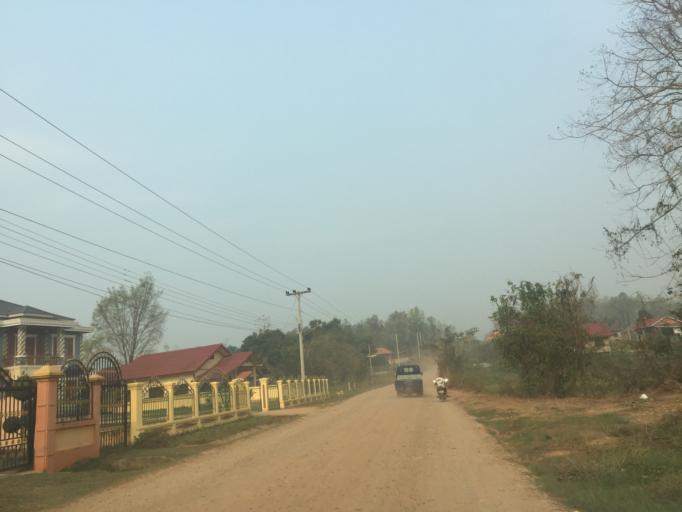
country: LA
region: Xiagnabouli
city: Sainyabuli
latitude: 19.2595
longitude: 101.6928
